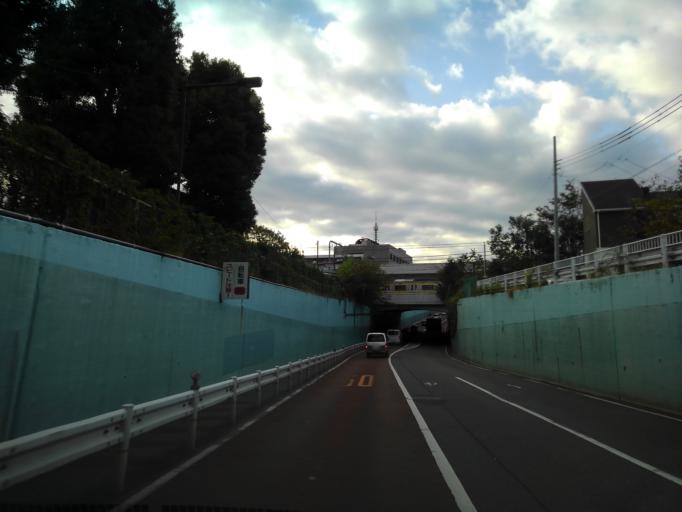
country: JP
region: Tokyo
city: Kokubunji
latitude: 35.7018
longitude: 139.4975
